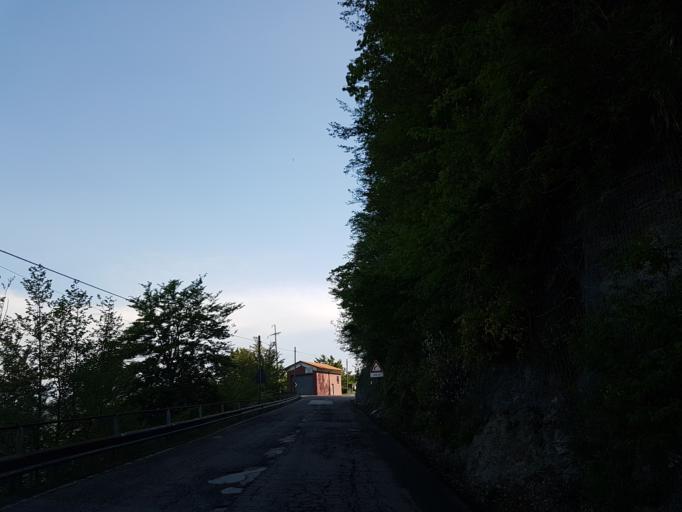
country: IT
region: Emilia-Romagna
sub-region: Forli-Cesena
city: San Piero in Bagno
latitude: 43.8097
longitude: 11.9202
